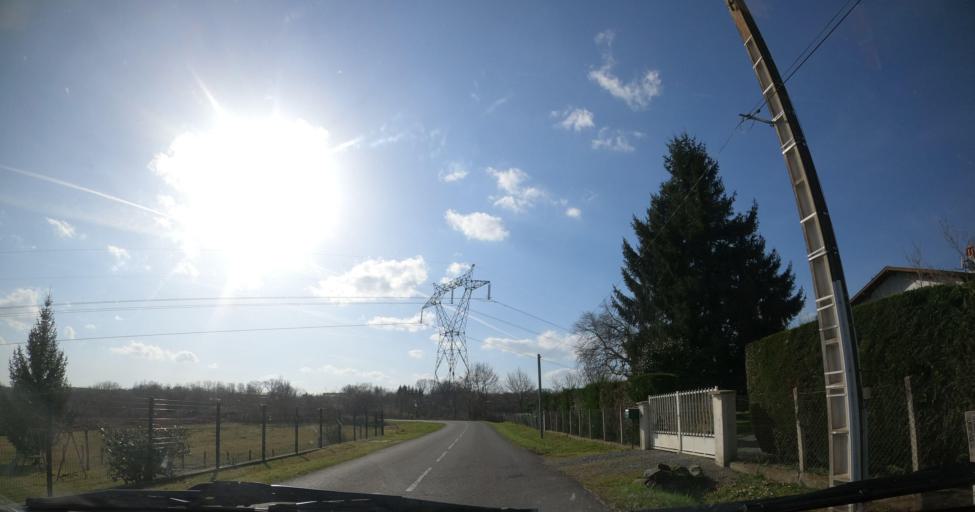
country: FR
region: Aquitaine
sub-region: Departement des Pyrenees-Atlantiques
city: Briscous
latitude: 43.4484
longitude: -1.3711
